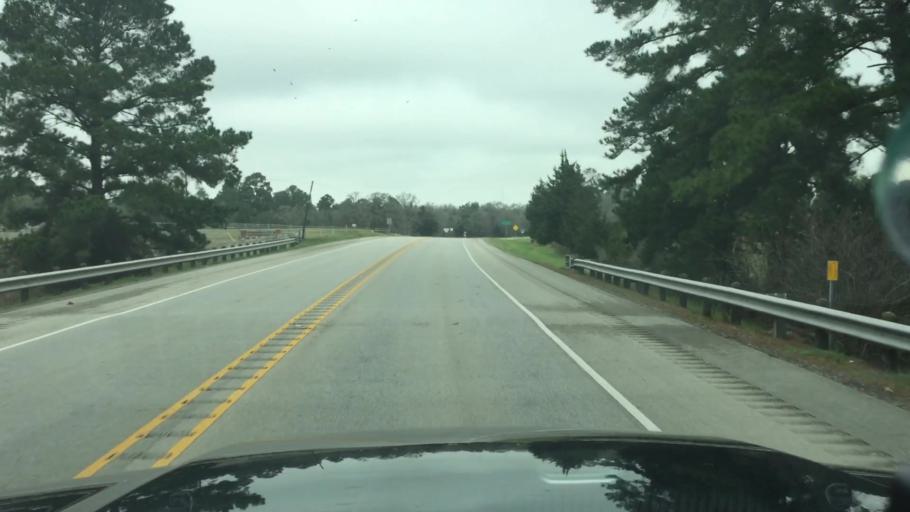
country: US
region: Texas
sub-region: Lee County
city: Giddings
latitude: 30.0799
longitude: -96.9172
